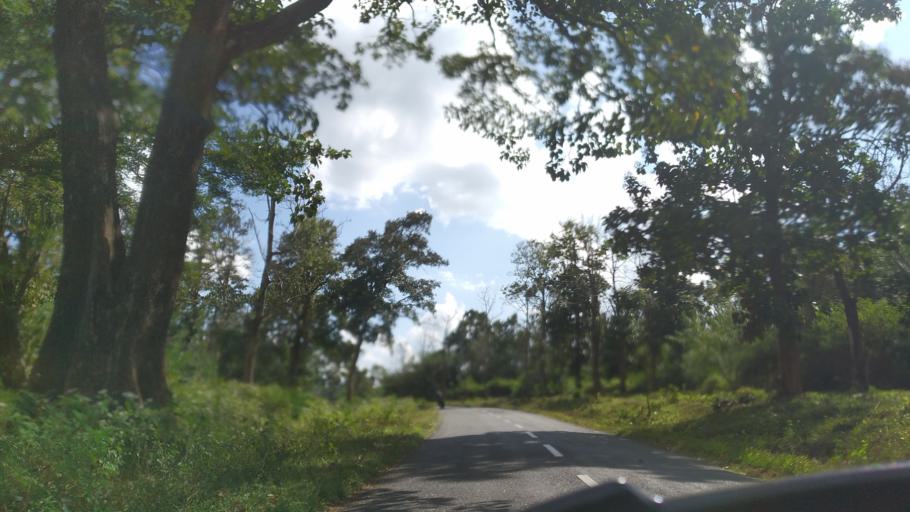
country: IN
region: Kerala
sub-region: Wayanad
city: Panamaram
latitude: 11.9275
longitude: 76.0654
